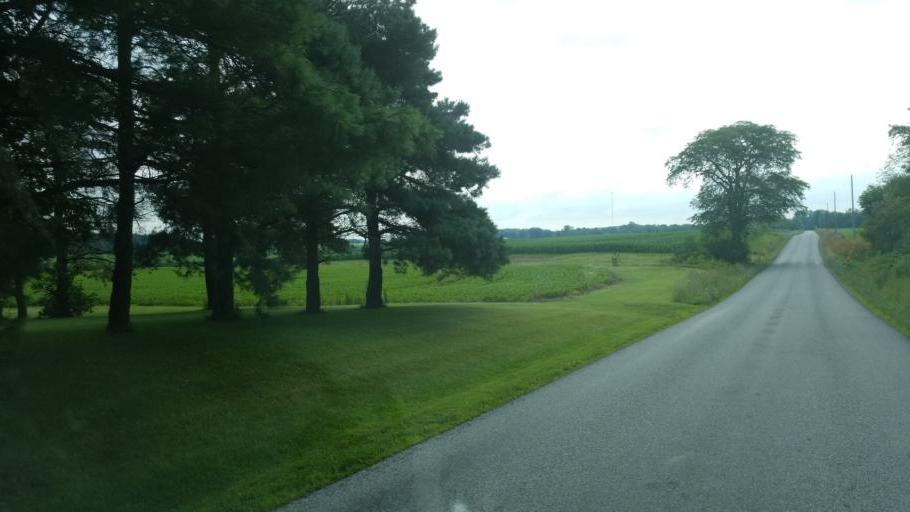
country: US
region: Ohio
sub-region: Knox County
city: Centerburg
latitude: 40.3196
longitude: -82.6853
